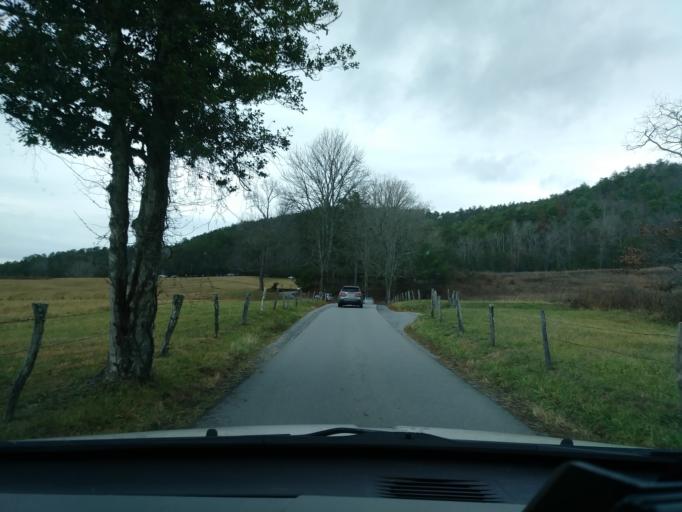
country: US
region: Tennessee
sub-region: Blount County
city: Wildwood
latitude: 35.6070
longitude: -83.8290
